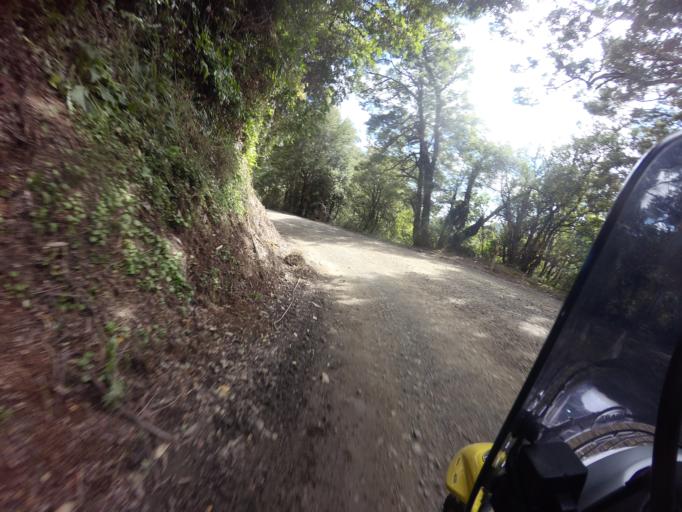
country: NZ
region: Bay of Plenty
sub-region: Whakatane District
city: Murupara
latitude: -38.6162
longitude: 177.0148
